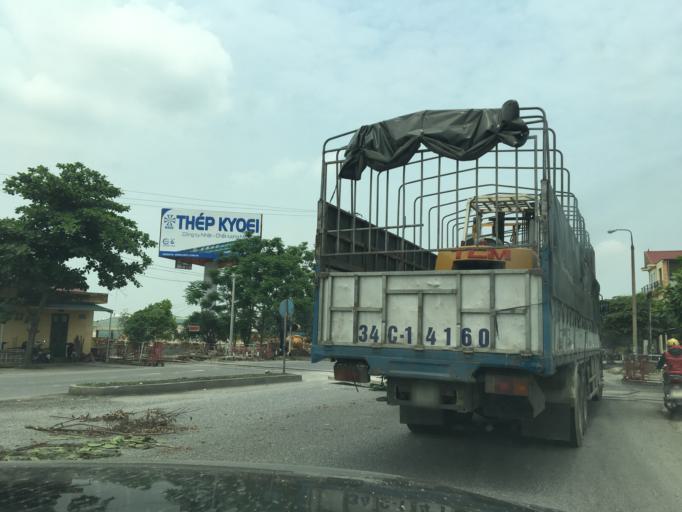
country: VN
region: Ninh Binh
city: Thanh Pho Ninh Binh
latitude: 20.2180
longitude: 105.9647
